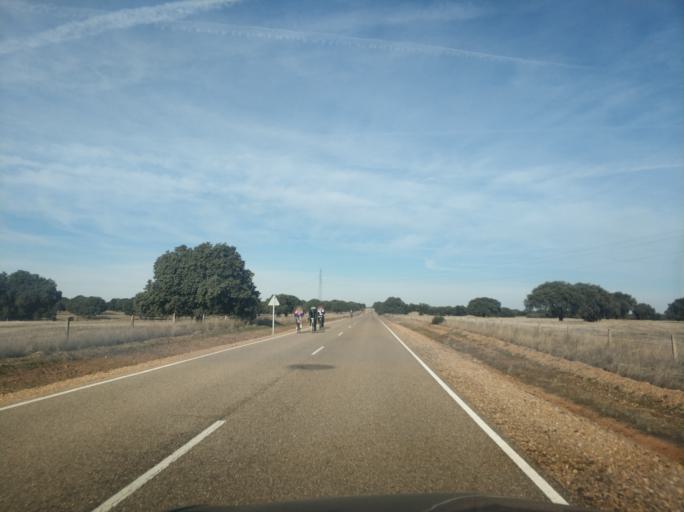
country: ES
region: Castille and Leon
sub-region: Provincia de Salamanca
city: Parada de Arriba
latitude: 40.9969
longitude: -5.8218
